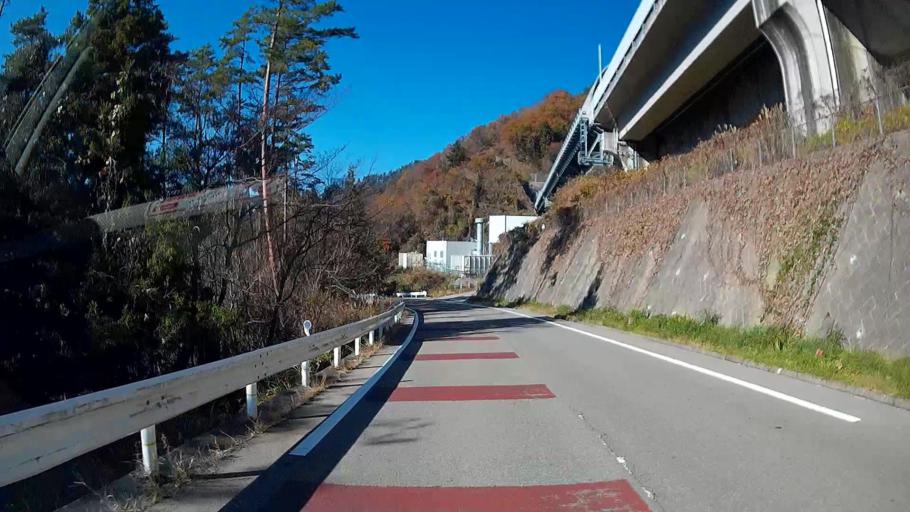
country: JP
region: Yamanashi
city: Otsuki
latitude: 35.5636
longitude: 139.0029
